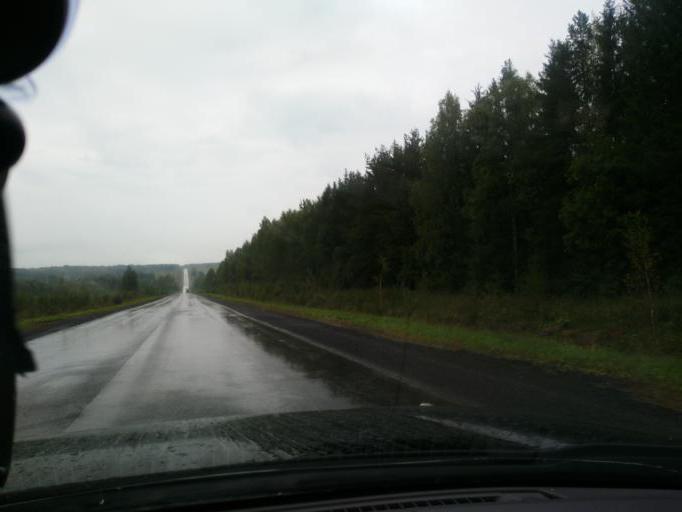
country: RU
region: Perm
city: Yugo-Kamskiy
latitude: 57.4758
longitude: 55.6785
